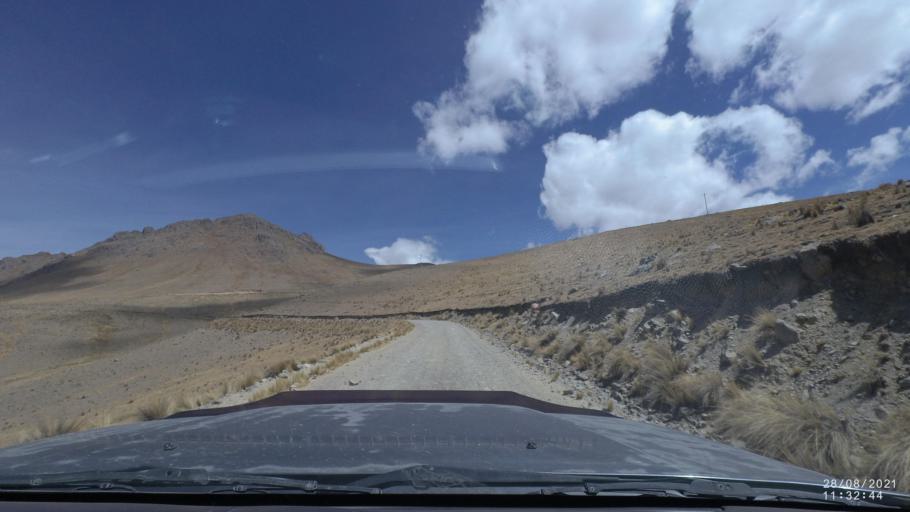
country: BO
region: Cochabamba
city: Sipe Sipe
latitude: -17.1834
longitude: -66.3676
